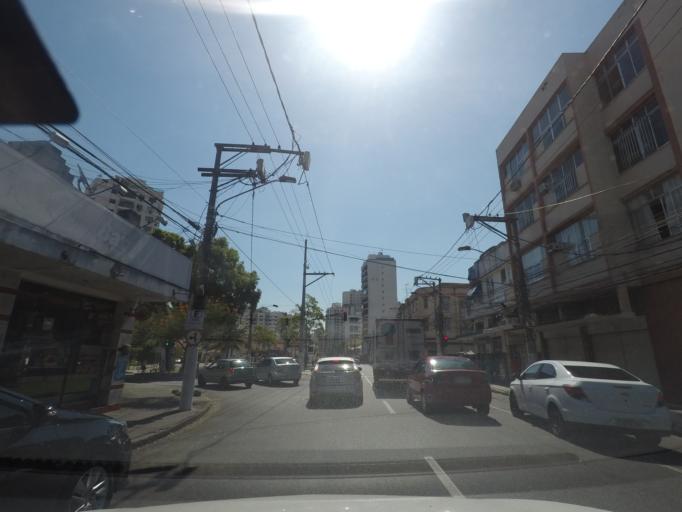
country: BR
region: Rio de Janeiro
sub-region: Niteroi
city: Niteroi
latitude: -22.8984
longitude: -43.1043
